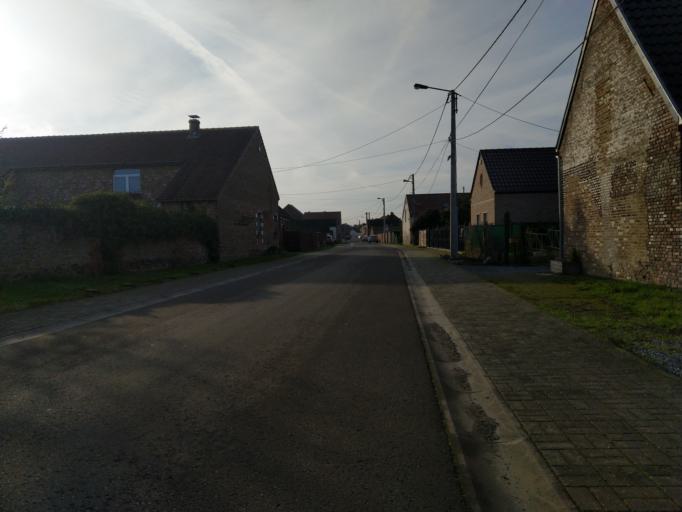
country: BE
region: Wallonia
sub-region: Province du Hainaut
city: Hensies
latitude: 50.4396
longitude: 3.6846
